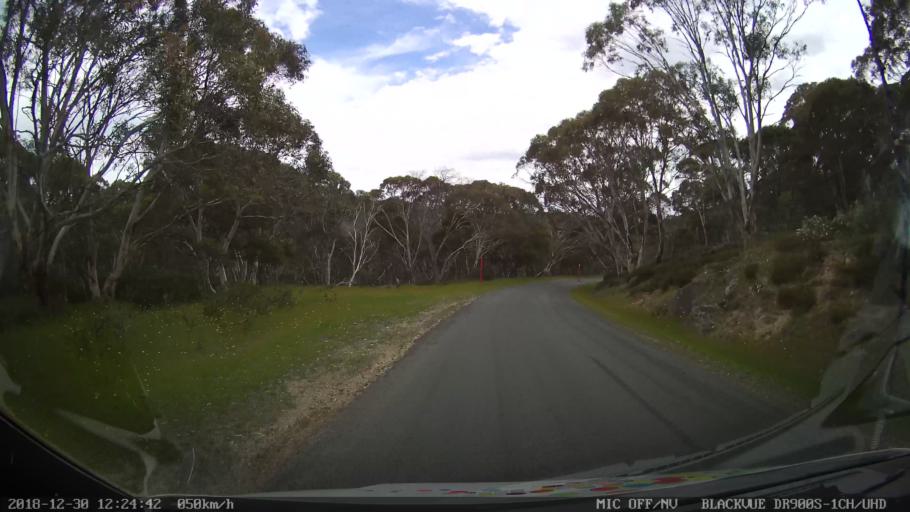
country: AU
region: New South Wales
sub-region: Snowy River
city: Jindabyne
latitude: -36.3548
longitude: 148.4905
